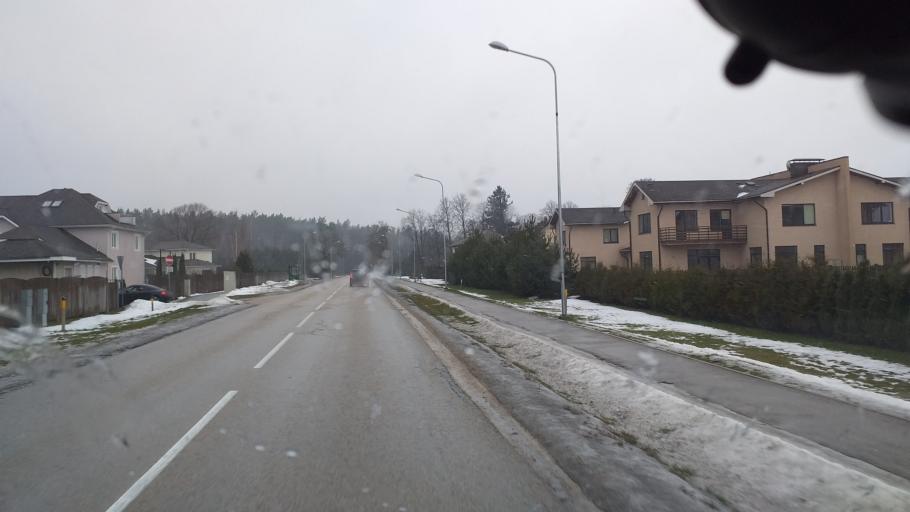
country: LV
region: Riga
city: Daugavgriva
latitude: 56.9850
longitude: 24.0027
